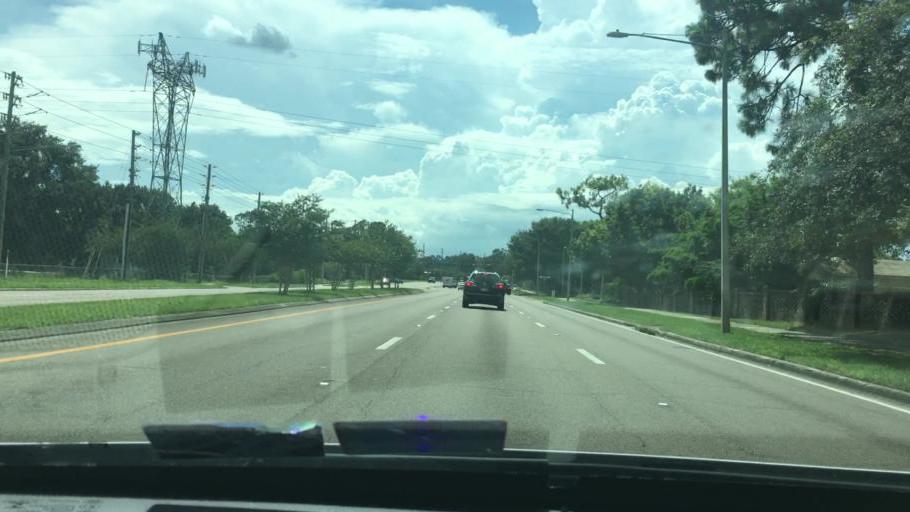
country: US
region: Florida
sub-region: Seminole County
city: Goldenrod
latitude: 28.5974
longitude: -81.2593
